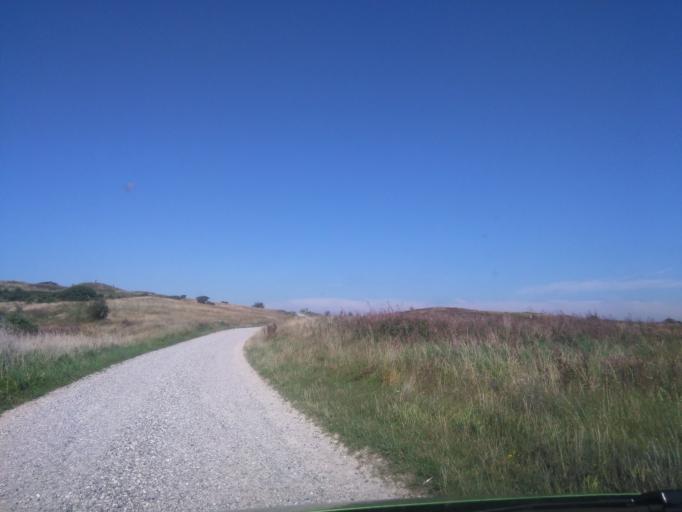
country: DK
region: Central Jutland
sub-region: Syddjurs Kommune
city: Ronde
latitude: 56.2018
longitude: 10.5318
